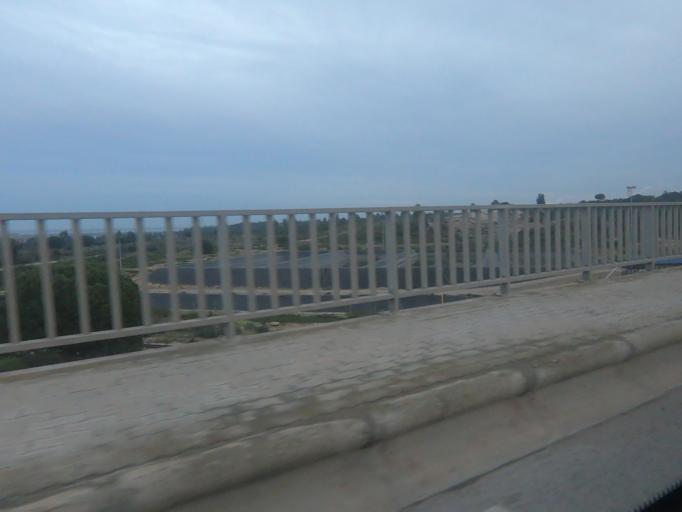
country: PT
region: Setubal
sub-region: Setubal
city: Setubal
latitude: 38.5054
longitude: -8.8305
